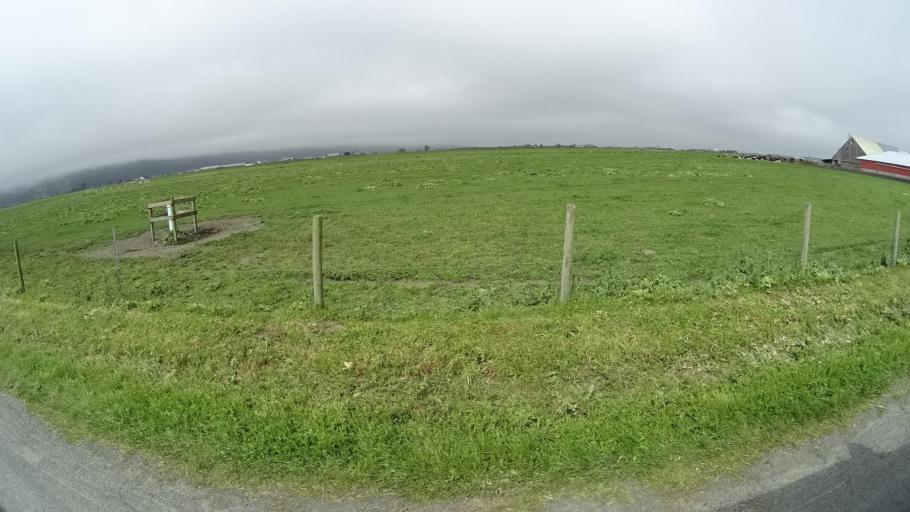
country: US
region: California
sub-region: Humboldt County
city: Fortuna
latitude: 40.5831
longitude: -124.1878
